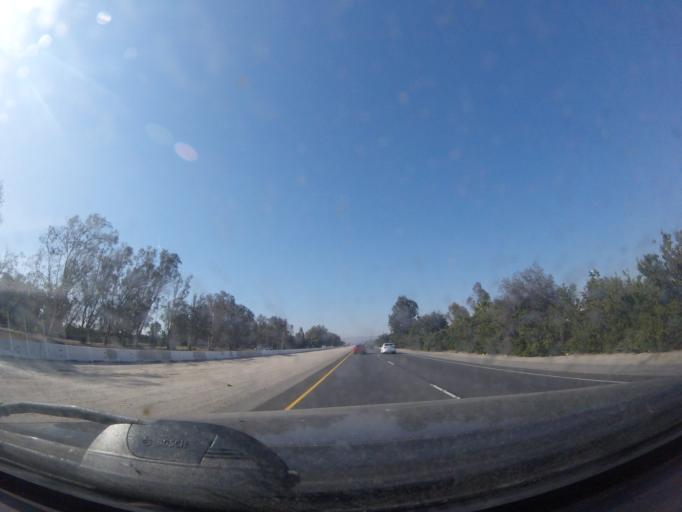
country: US
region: California
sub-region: San Bernardino County
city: Redlands
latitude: 34.0892
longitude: -117.2008
